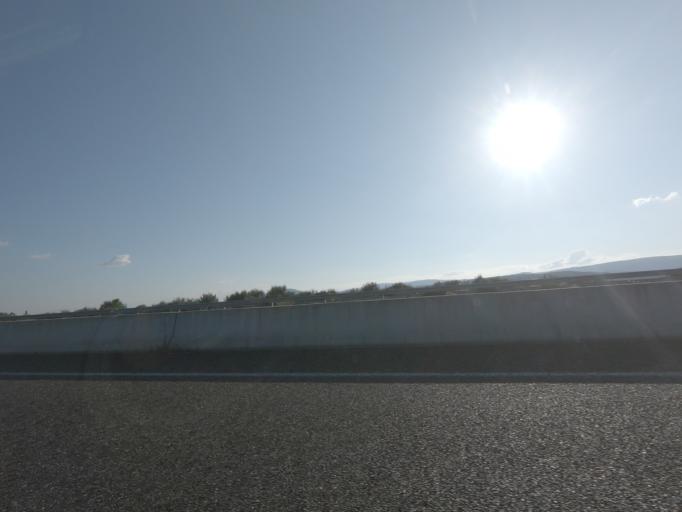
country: ES
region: Galicia
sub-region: Provincia de Ourense
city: Oimbra
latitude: 41.8322
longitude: -7.4216
